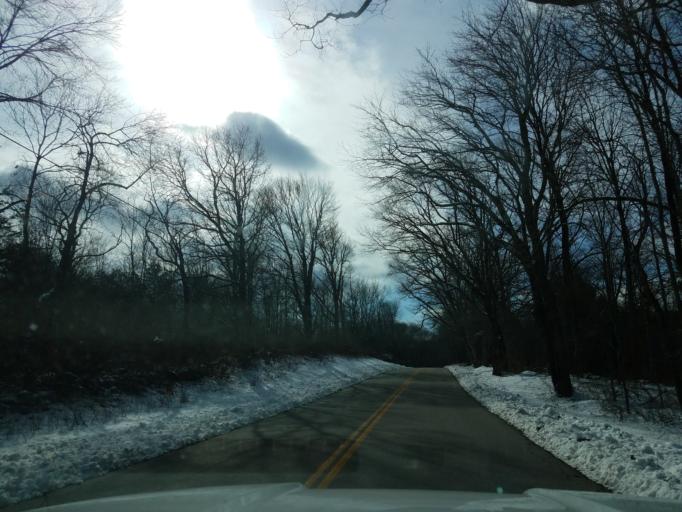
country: US
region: Connecticut
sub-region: New London County
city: Colchester
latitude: 41.5963
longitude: -72.3518
